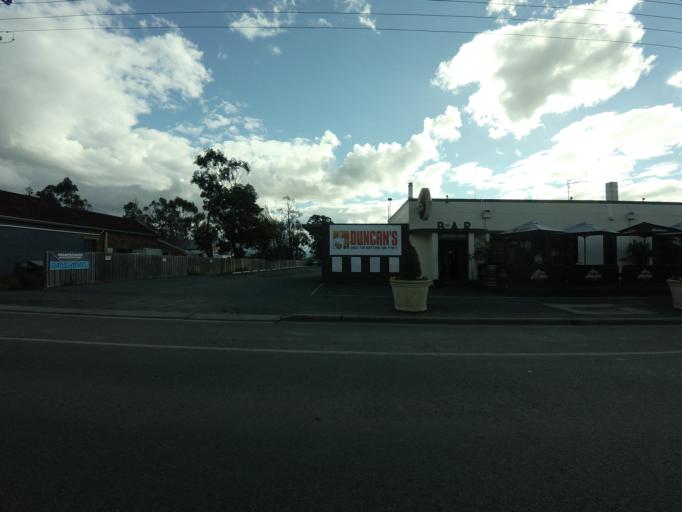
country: AU
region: Tasmania
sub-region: Northern Midlands
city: Longford
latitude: -41.6856
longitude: 147.0804
